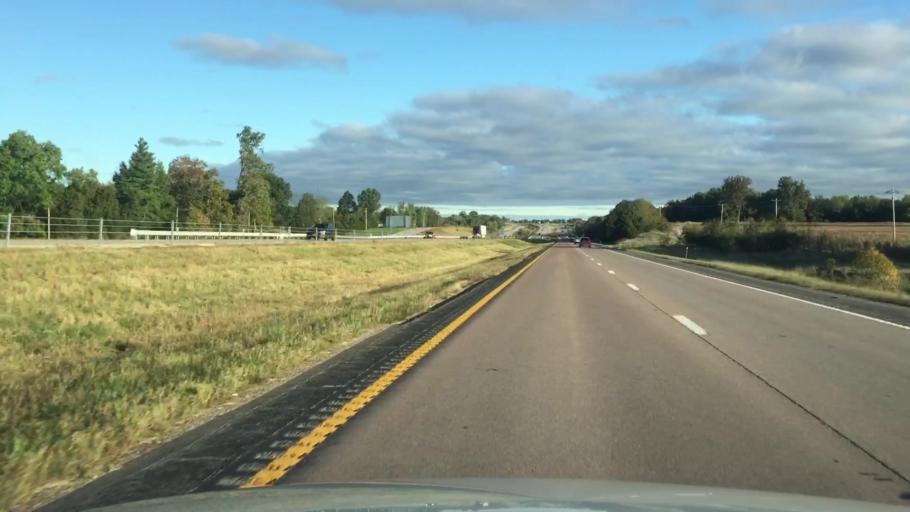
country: US
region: Missouri
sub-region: Boone County
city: Ashland
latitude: 38.8461
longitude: -92.2491
